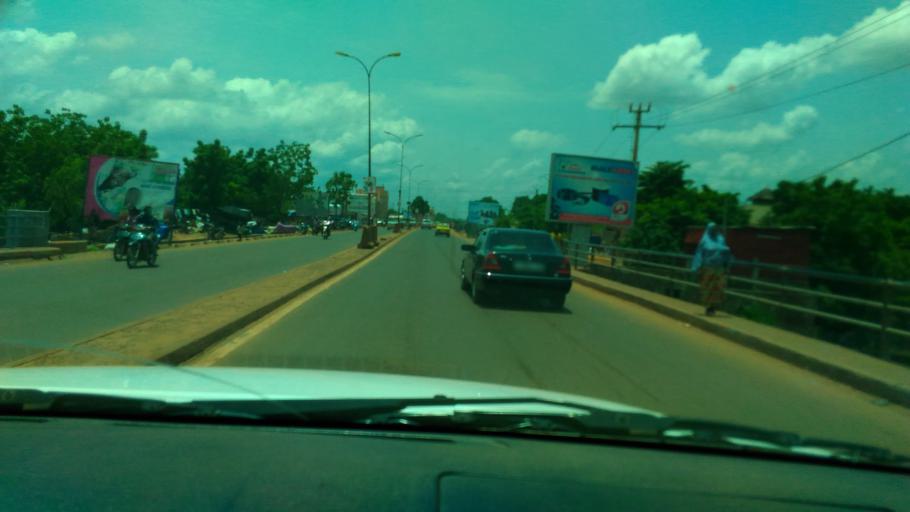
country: ML
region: Bamako
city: Bamako
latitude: 12.6599
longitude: -7.9607
